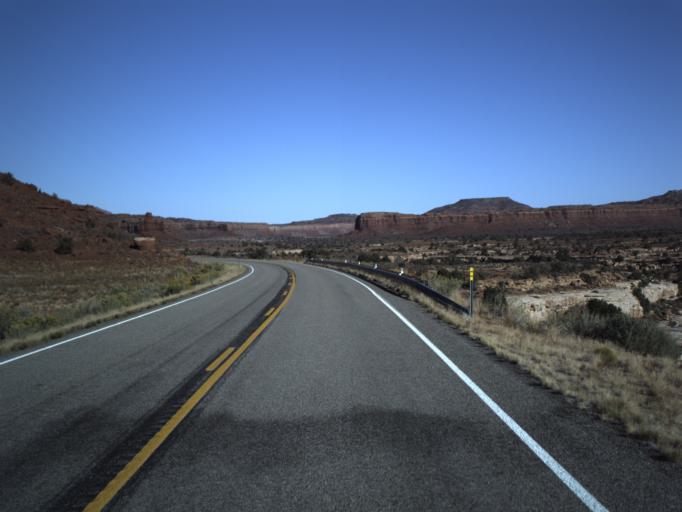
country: US
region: Utah
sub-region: San Juan County
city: Blanding
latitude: 37.6877
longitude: -110.2232
